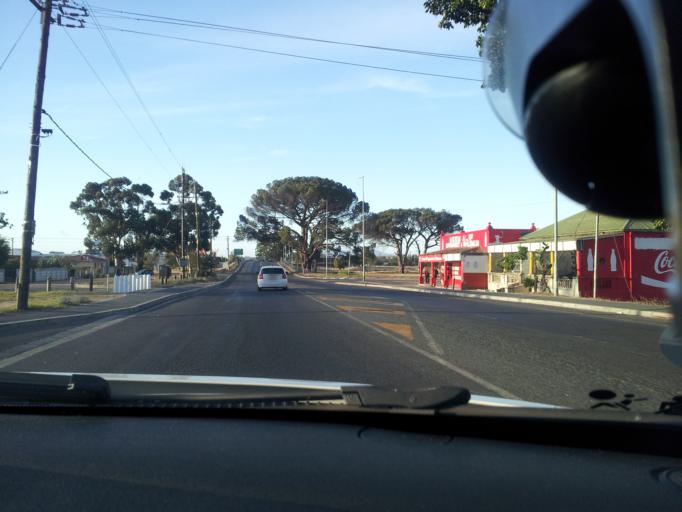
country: ZA
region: Western Cape
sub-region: Cape Winelands District Municipality
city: Paarl
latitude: -33.8073
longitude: 18.8738
